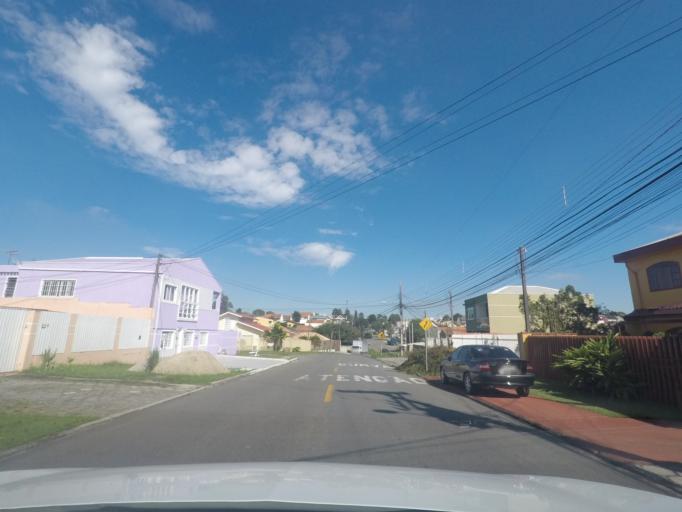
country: BR
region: Parana
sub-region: Sao Jose Dos Pinhais
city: Sao Jose dos Pinhais
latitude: -25.5074
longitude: -49.2594
